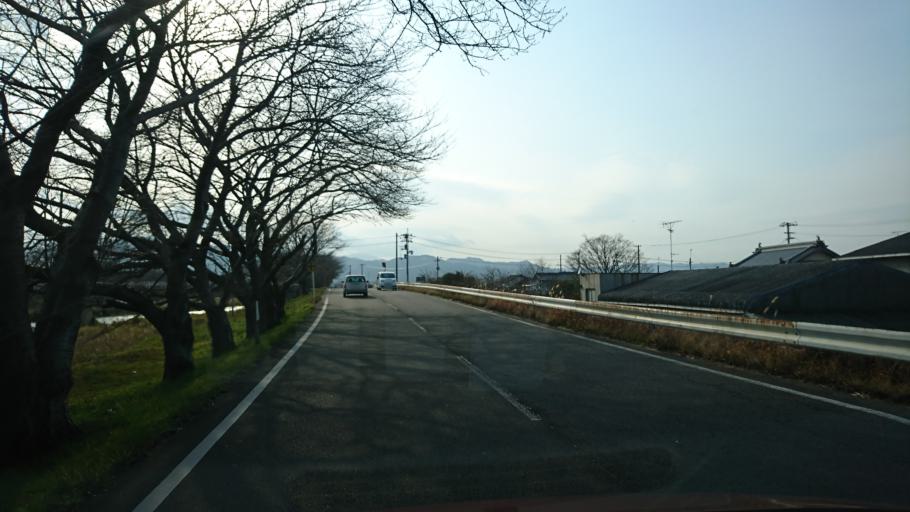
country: JP
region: Ehime
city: Saijo
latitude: 34.0359
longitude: 133.0222
